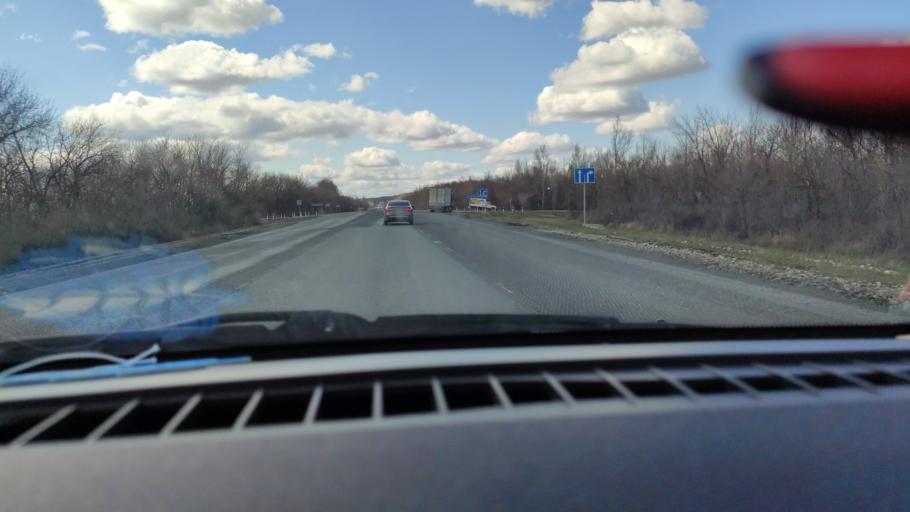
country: RU
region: Saratov
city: Dukhovnitskoye
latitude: 52.6603
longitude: 48.2102
